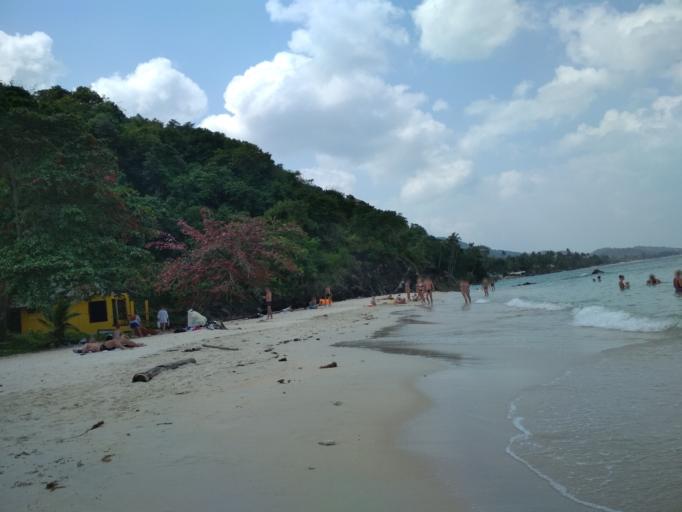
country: TH
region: Surat Thani
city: Ko Samui
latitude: 9.5822
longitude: 99.9661
